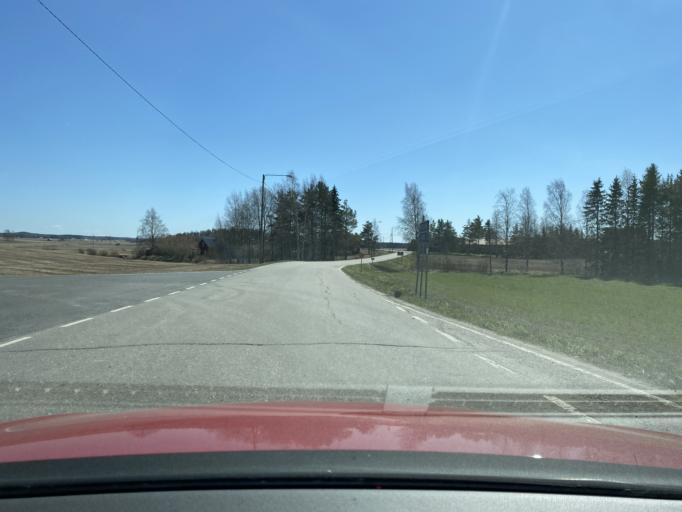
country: FI
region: Pirkanmaa
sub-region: Lounais-Pirkanmaa
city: Punkalaidun
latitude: 61.0506
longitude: 23.1927
